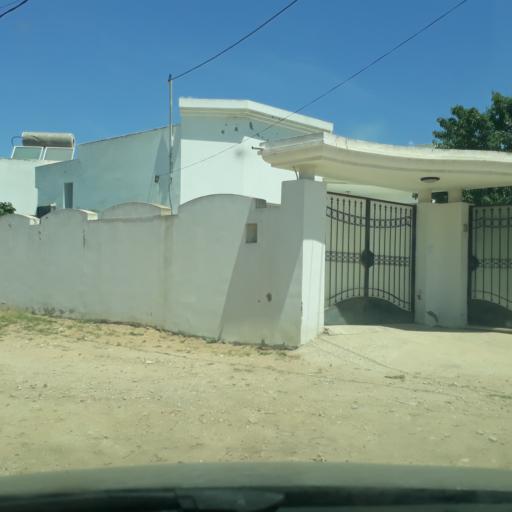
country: TN
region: Safaqis
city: Al Qarmadah
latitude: 34.8179
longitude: 10.7533
